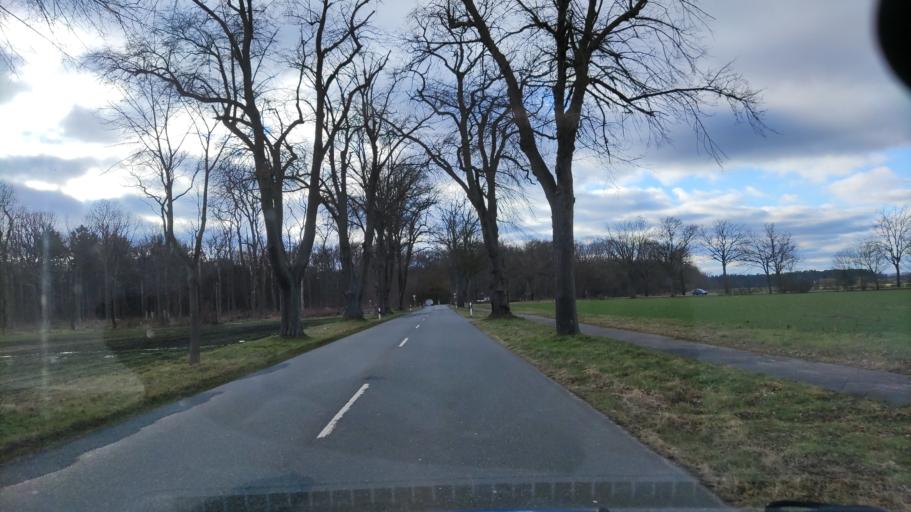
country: DE
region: Lower Saxony
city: Klein Gusborn
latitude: 53.1047
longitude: 11.1815
